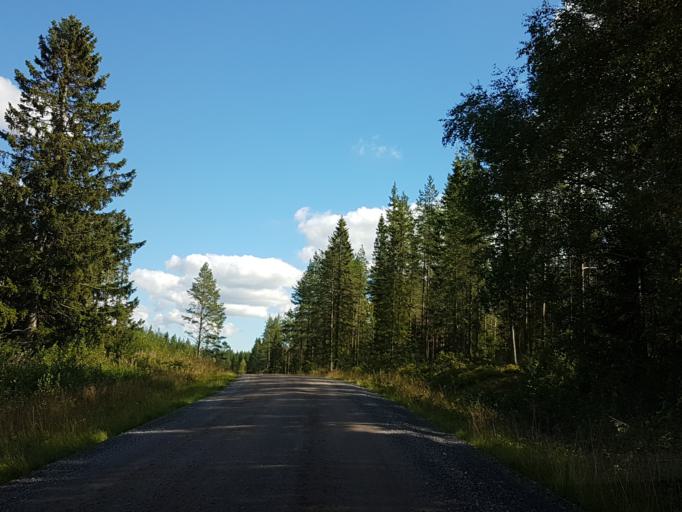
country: SE
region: Vaesterbotten
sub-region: Skelleftea Kommun
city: Burtraesk
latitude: 64.2974
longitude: 20.4916
